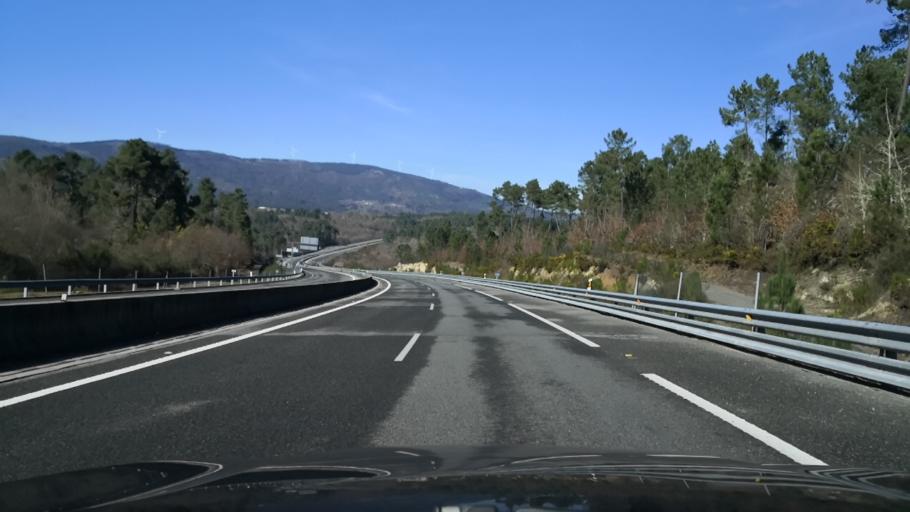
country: ES
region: Galicia
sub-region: Provincia de Ourense
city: Cea
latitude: 42.4587
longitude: -8.0234
